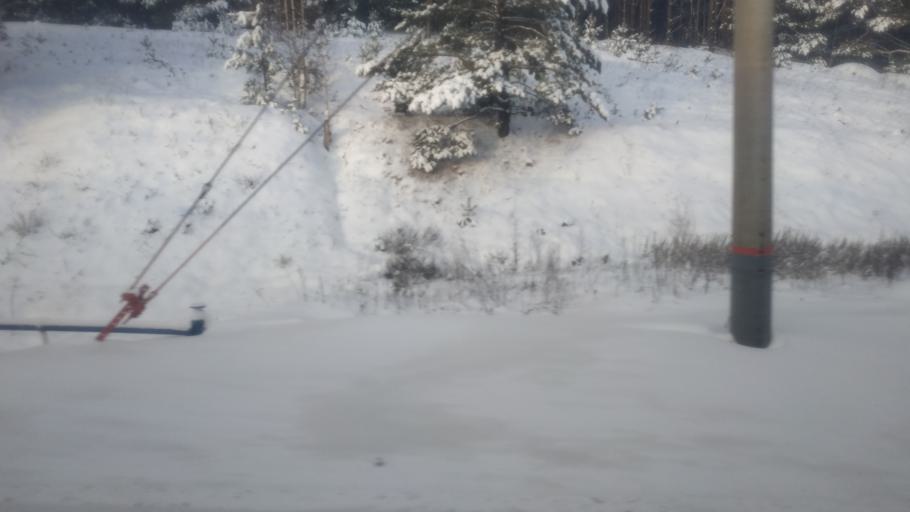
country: RU
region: Kirov
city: Krasnaya Polyana
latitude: 56.2485
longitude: 51.2032
